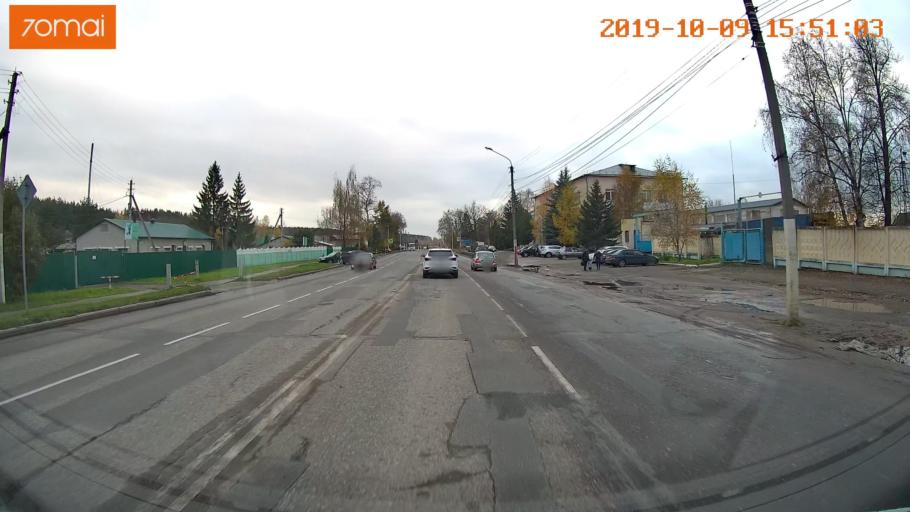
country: RU
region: Kostroma
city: Oktyabr'skiy
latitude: 57.7999
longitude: 40.9826
